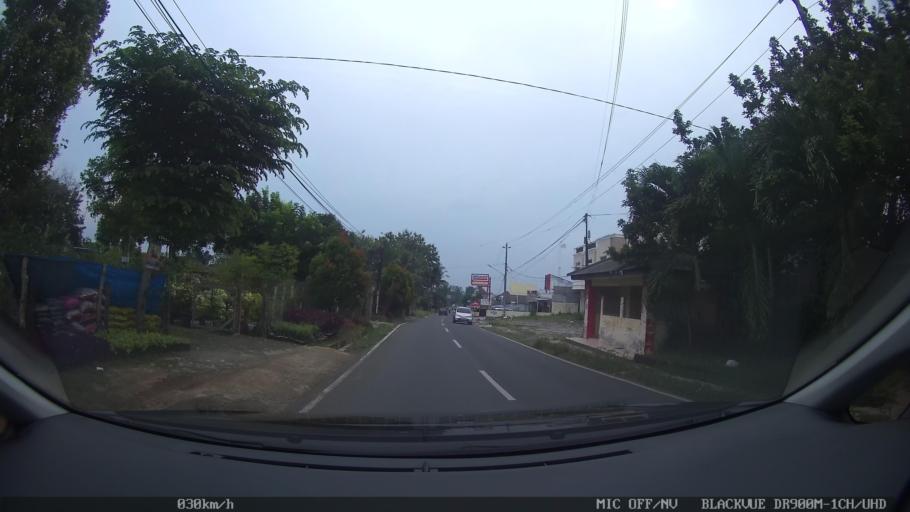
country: ID
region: Lampung
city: Kedaton
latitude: -5.3883
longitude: 105.2403
